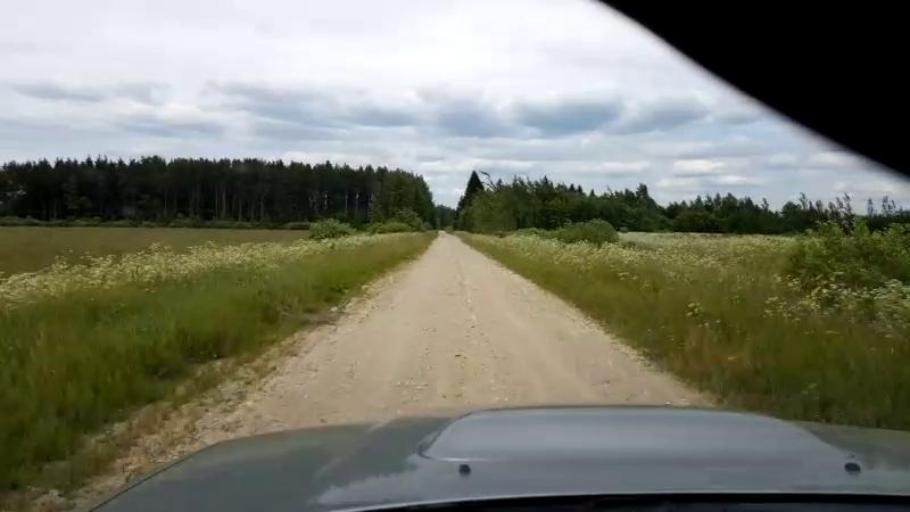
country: EE
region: Paernumaa
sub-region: Sauga vald
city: Sauga
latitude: 58.5003
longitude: 24.5808
